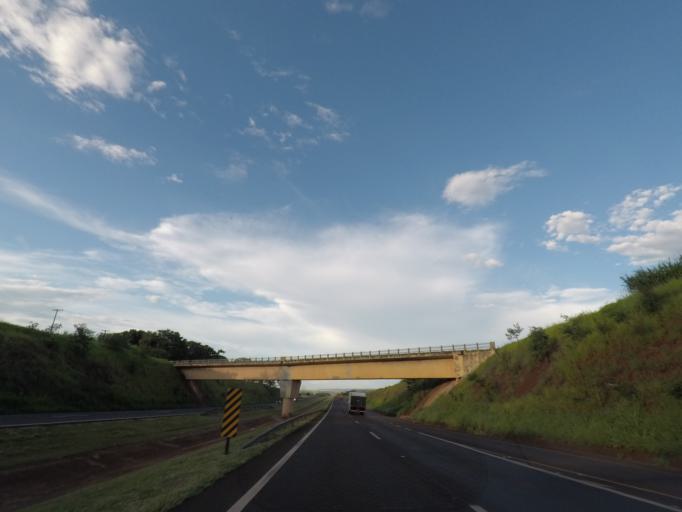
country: BR
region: Sao Paulo
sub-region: Ituverava
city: Ituverava
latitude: -20.3264
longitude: -47.8038
